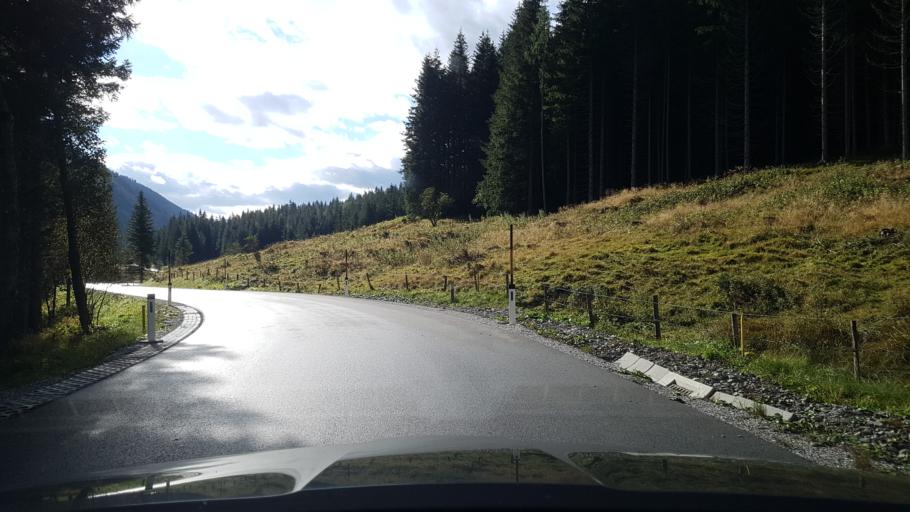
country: AT
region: Styria
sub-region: Politischer Bezirk Murau
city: Schoder
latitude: 47.2327
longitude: 14.0882
